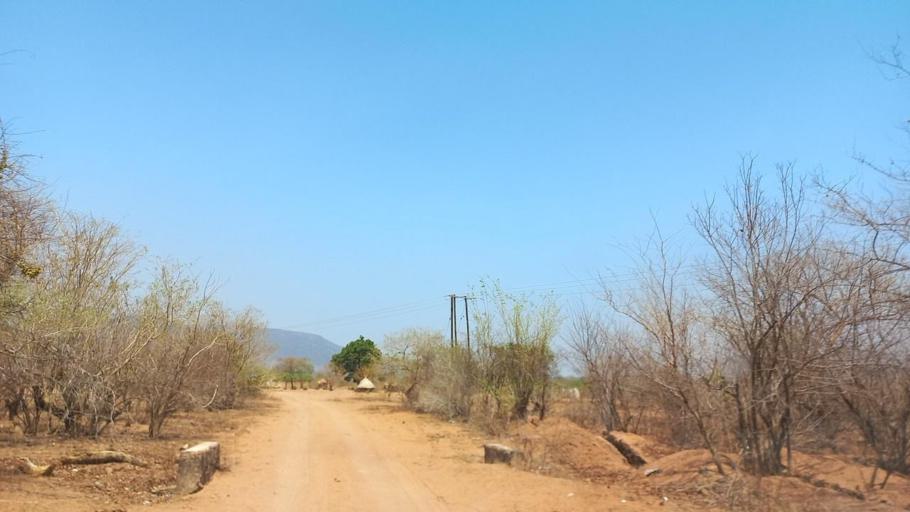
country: ZM
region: Lusaka
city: Luangwa
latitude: -15.5908
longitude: 30.3889
